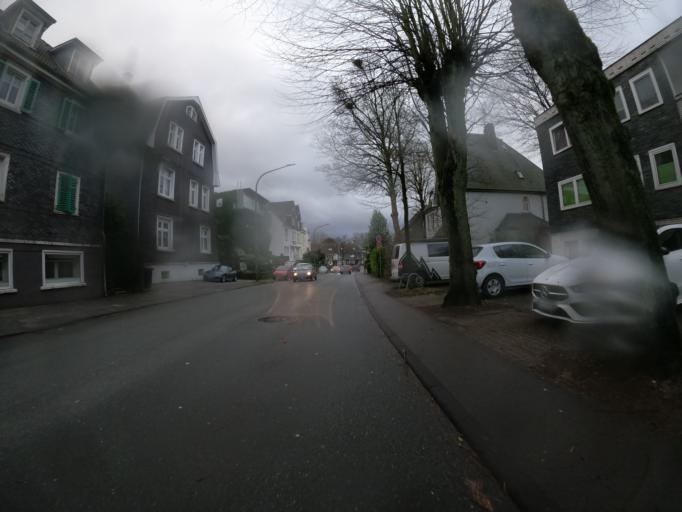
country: DE
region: North Rhine-Westphalia
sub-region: Regierungsbezirk Dusseldorf
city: Solingen
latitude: 51.2043
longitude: 7.1307
